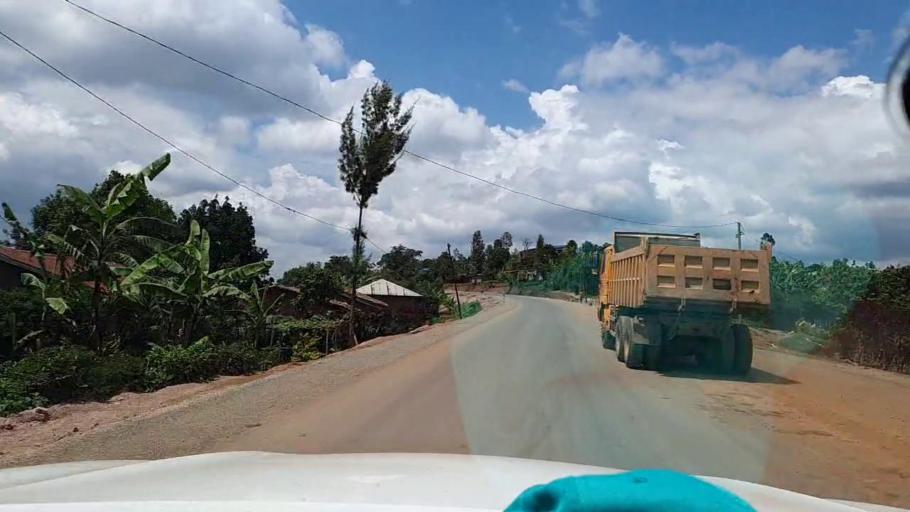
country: RW
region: Southern Province
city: Nzega
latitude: -2.6458
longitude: 29.5711
